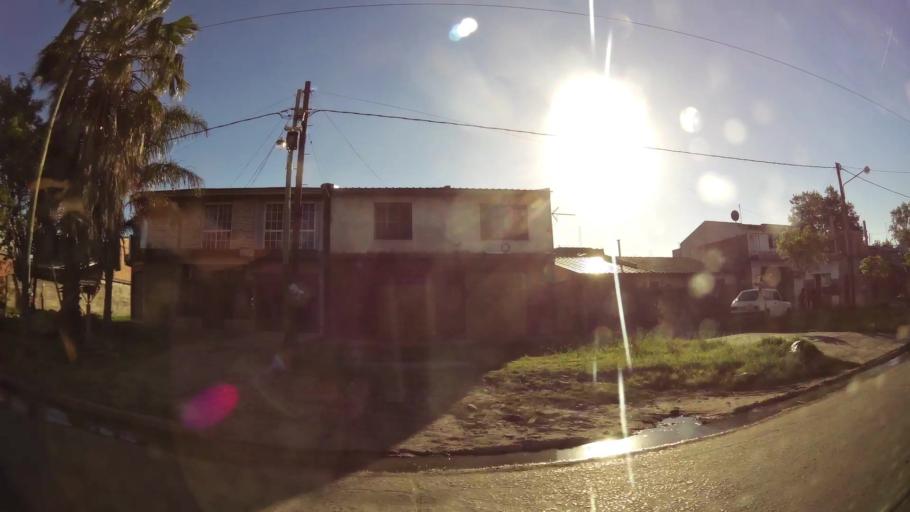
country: AR
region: Buenos Aires
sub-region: Partido de Almirante Brown
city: Adrogue
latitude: -34.7552
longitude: -58.3362
